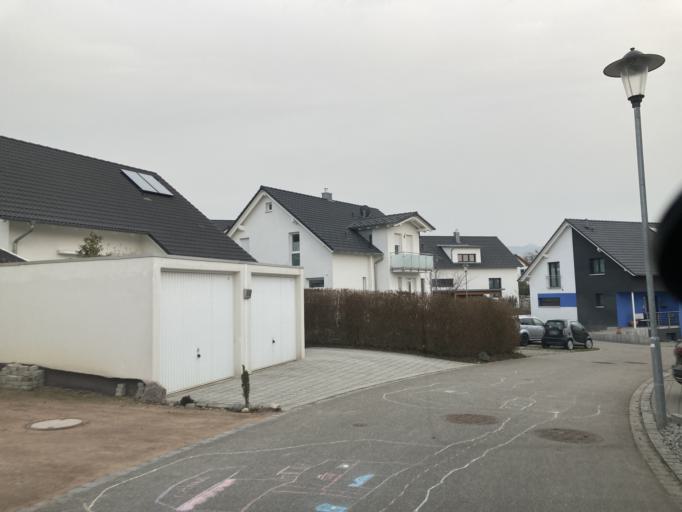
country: DE
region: Baden-Wuerttemberg
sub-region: Freiburg Region
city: Mullheim
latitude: 47.8134
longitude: 7.6376
